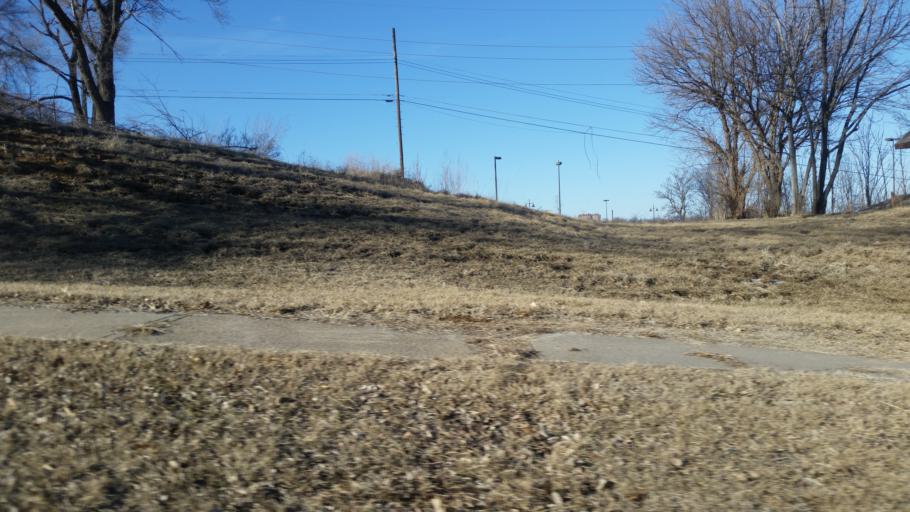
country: US
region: Nebraska
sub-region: Douglas County
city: Omaha
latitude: 41.2230
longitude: -95.9318
